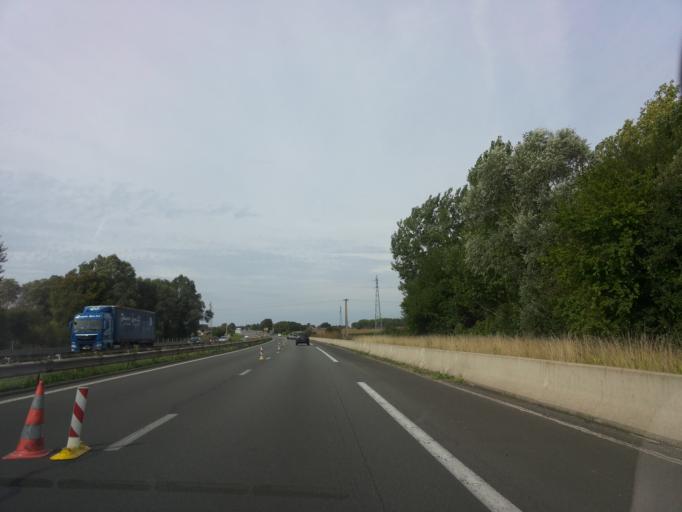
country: FR
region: Nord-Pas-de-Calais
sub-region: Departement du Pas-de-Calais
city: Labourse
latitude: 50.4969
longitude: 2.6744
